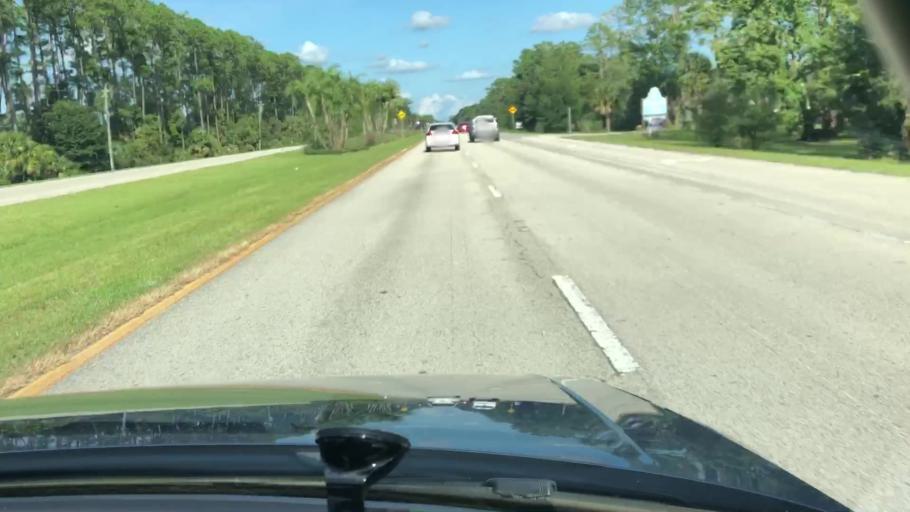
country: US
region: Florida
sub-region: Volusia County
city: South Daytona
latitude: 29.1608
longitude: -81.0630
